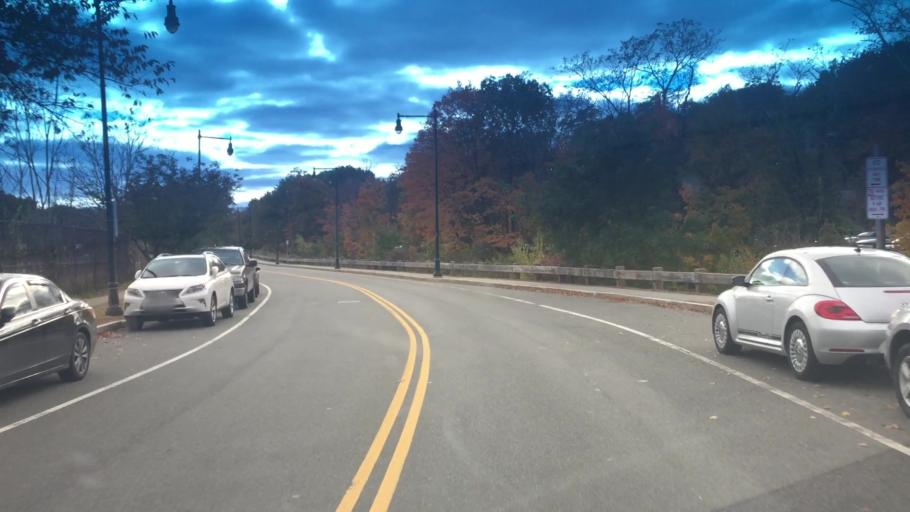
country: US
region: Massachusetts
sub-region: Middlesex County
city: Winchester
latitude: 42.4503
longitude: -71.1373
